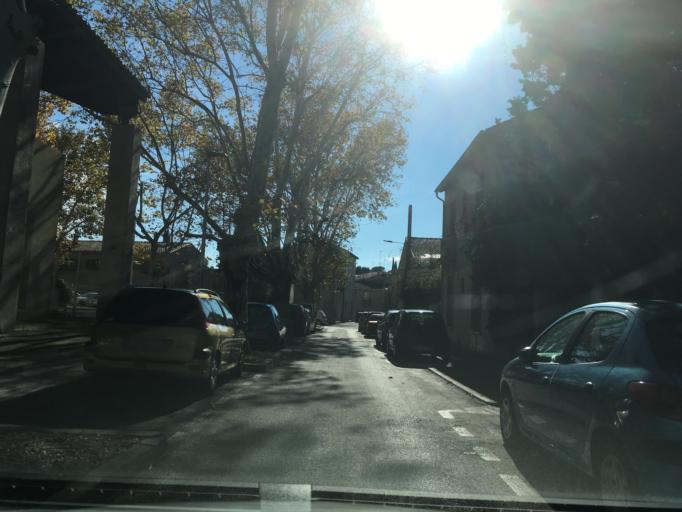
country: FR
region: Languedoc-Roussillon
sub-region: Departement de l'Herault
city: Juvignac
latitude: 43.6129
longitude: 3.8304
